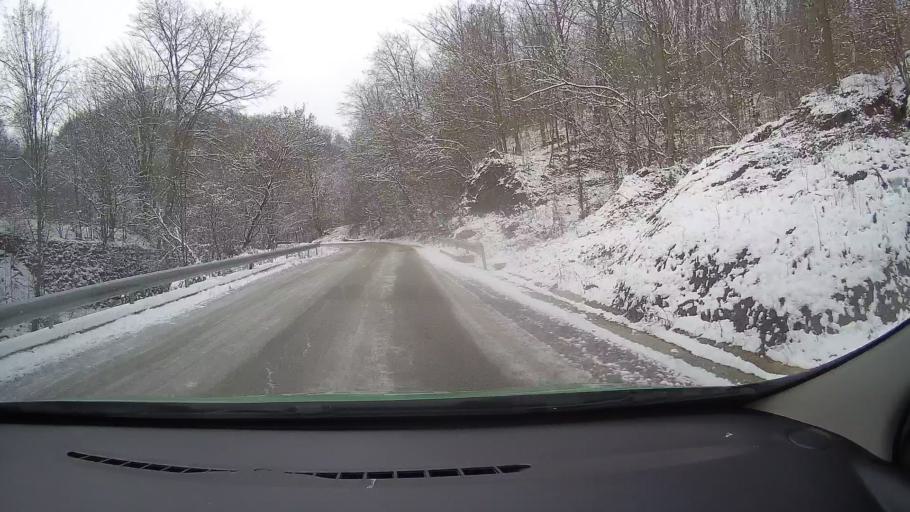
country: RO
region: Alba
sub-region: Oras Zlatna
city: Zlatna
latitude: 46.0963
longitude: 23.1773
